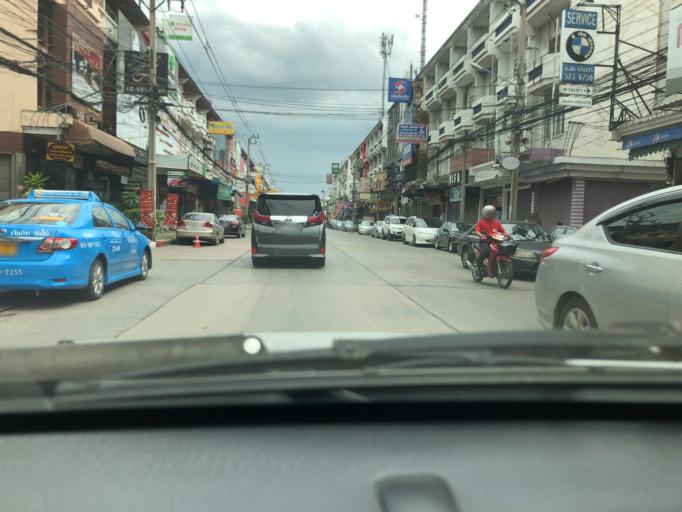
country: TH
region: Nonthaburi
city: Pak Kret
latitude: 13.9065
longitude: 100.5379
